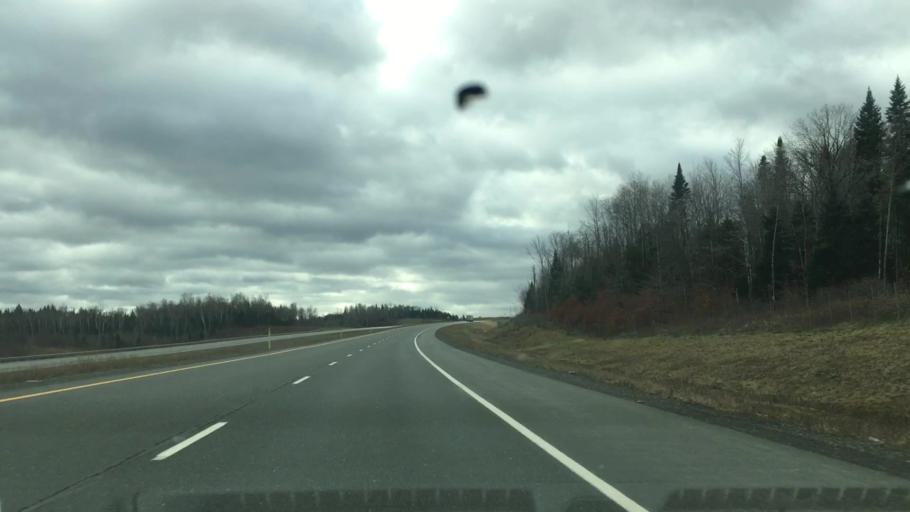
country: US
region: Maine
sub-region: Aroostook County
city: Fort Fairfield
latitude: 46.6665
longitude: -67.7301
